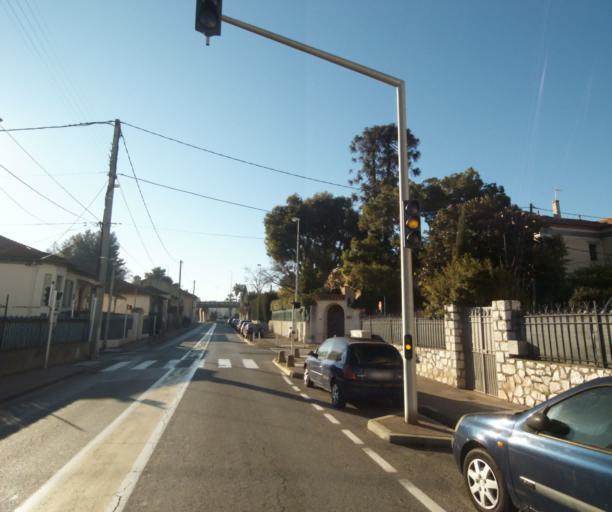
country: FR
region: Provence-Alpes-Cote d'Azur
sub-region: Departement des Alpes-Maritimes
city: Antibes
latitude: 43.5823
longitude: 7.1162
